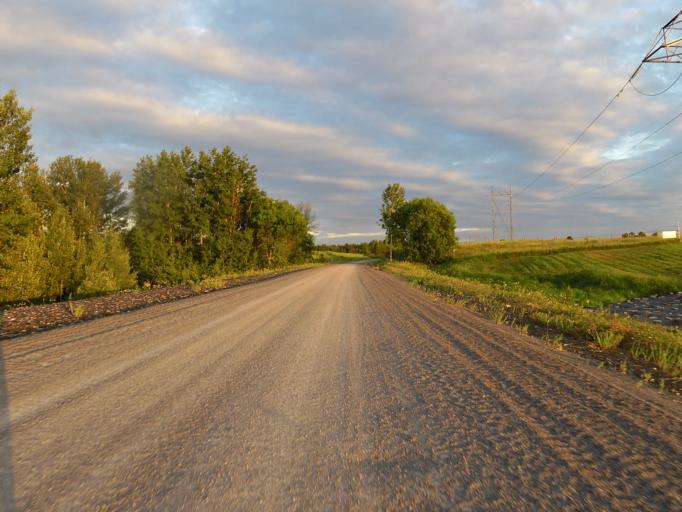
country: CA
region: Ontario
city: Arnprior
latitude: 45.4006
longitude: -76.3236
